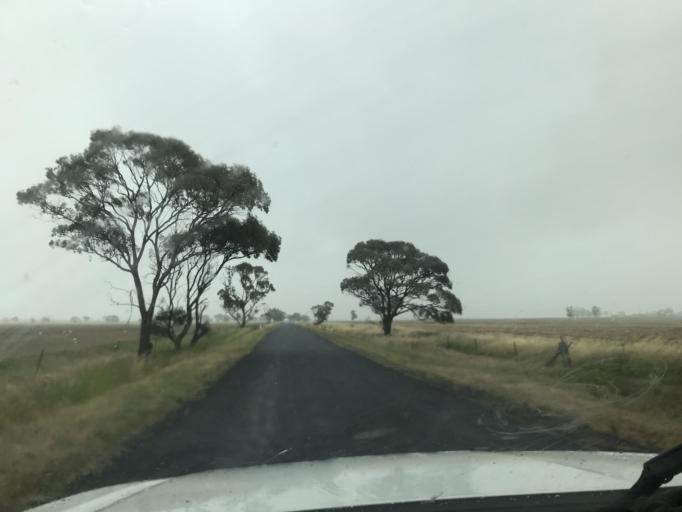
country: AU
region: South Australia
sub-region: Tatiara
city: Bordertown
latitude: -36.3140
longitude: 141.1544
